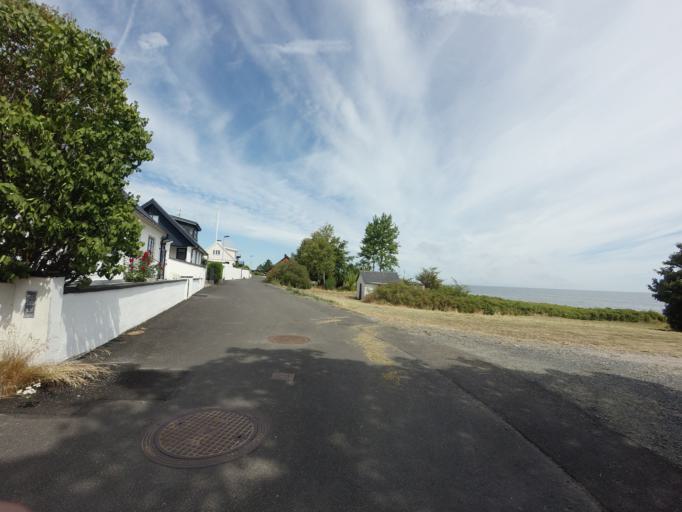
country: SE
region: Skane
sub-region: Simrishamns Kommun
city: Simrishamn
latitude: 55.5437
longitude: 14.3571
